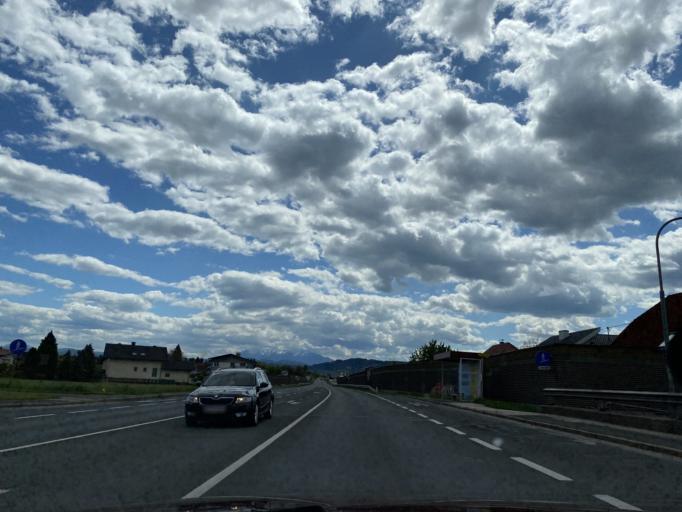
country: AT
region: Carinthia
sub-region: Politischer Bezirk Wolfsberg
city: Wolfsberg
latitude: 46.8096
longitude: 14.8315
